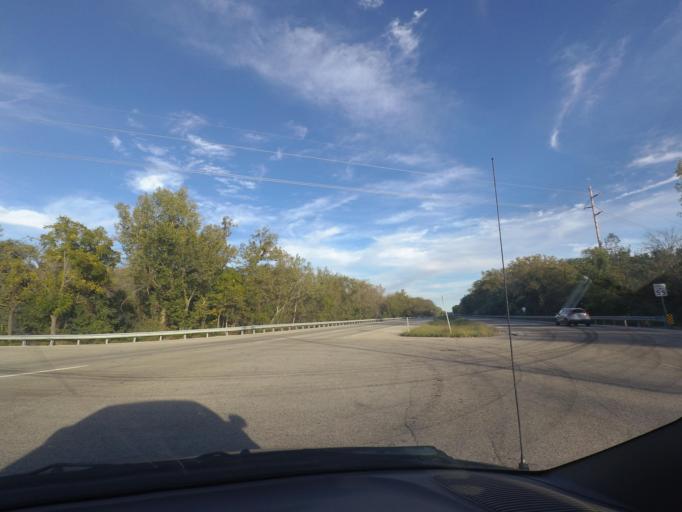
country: US
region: Illinois
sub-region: Sangamon County
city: Grandview
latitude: 39.7829
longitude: -89.5937
